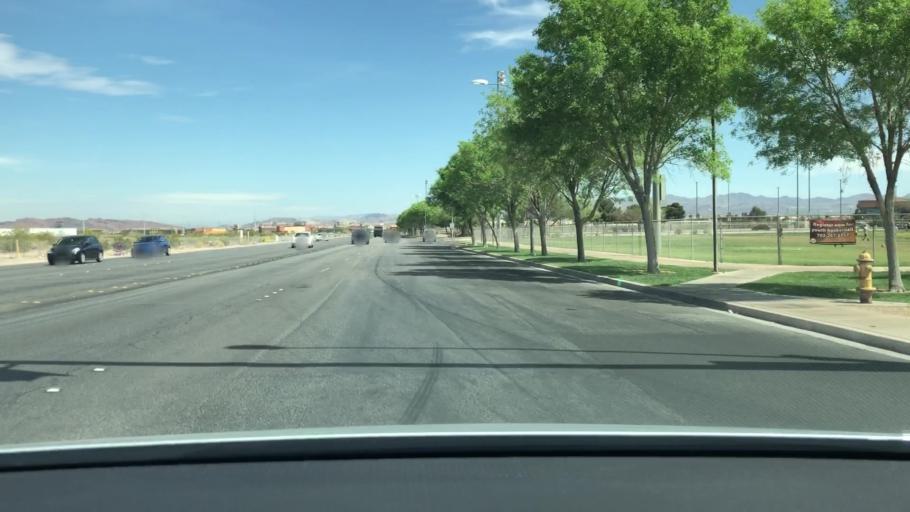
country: US
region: Nevada
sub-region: Clark County
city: Whitney
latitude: 36.0838
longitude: -115.0436
